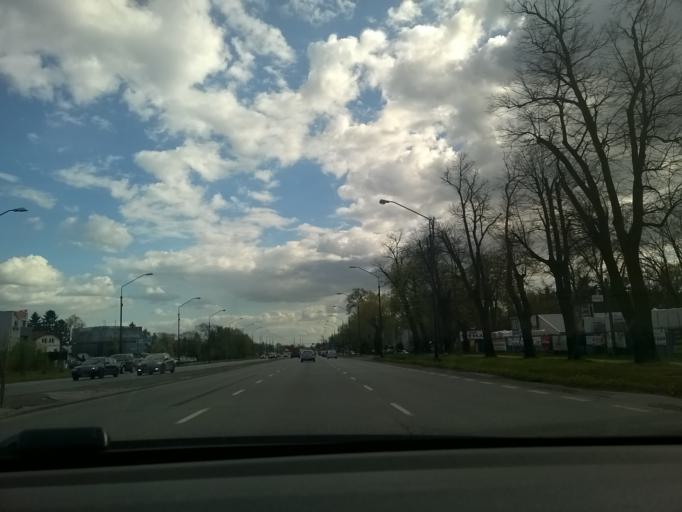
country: PL
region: Masovian Voivodeship
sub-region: Powiat piaseczynski
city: Mysiadlo
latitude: 52.1144
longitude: 21.0183
